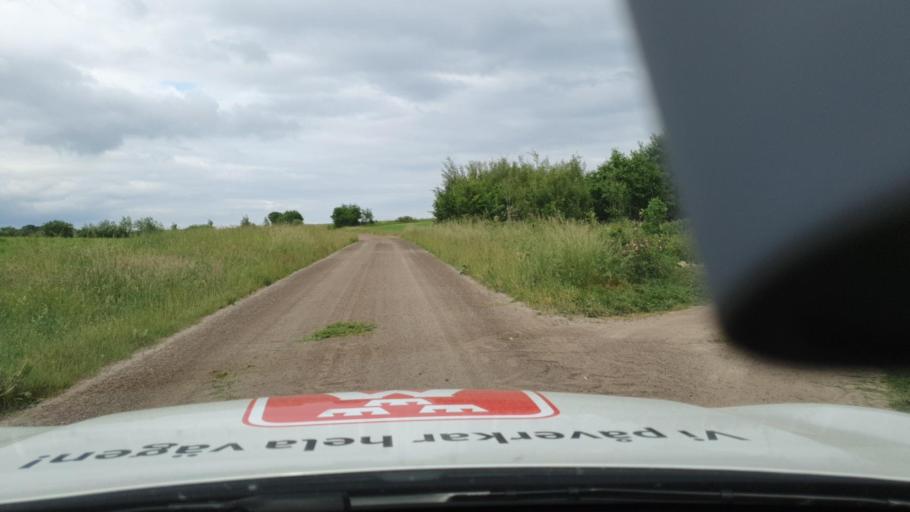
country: SE
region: Vaestra Goetaland
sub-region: Hjo Kommun
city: Hjo
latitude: 58.2149
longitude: 14.1935
